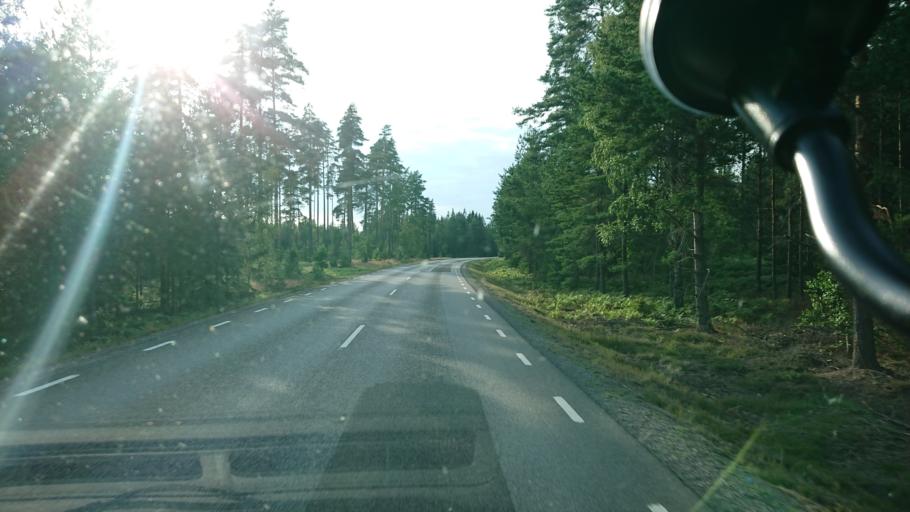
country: SE
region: Kronoberg
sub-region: Vaxjo Kommun
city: Rottne
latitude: 57.0269
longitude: 14.9797
